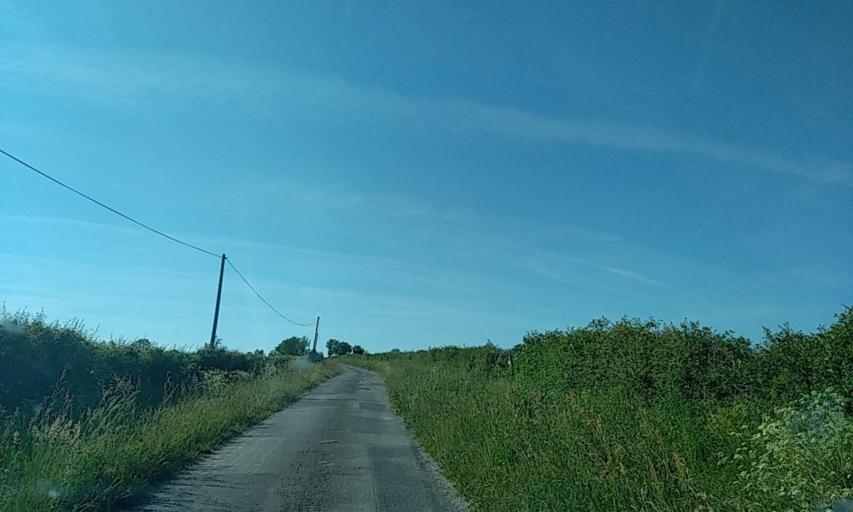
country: FR
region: Poitou-Charentes
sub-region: Departement des Deux-Sevres
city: Boisme
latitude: 46.7997
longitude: -0.4229
